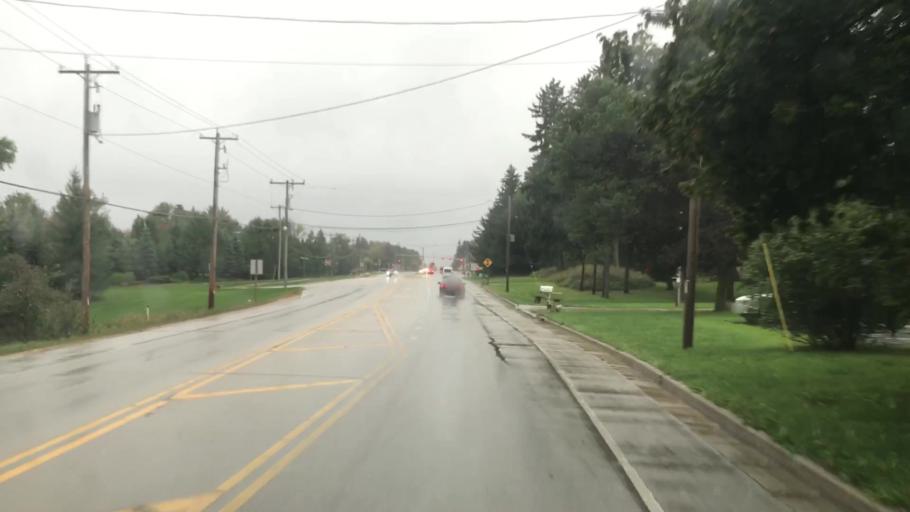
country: US
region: Wisconsin
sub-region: Ozaukee County
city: Mequon
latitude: 43.2249
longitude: -88.0037
